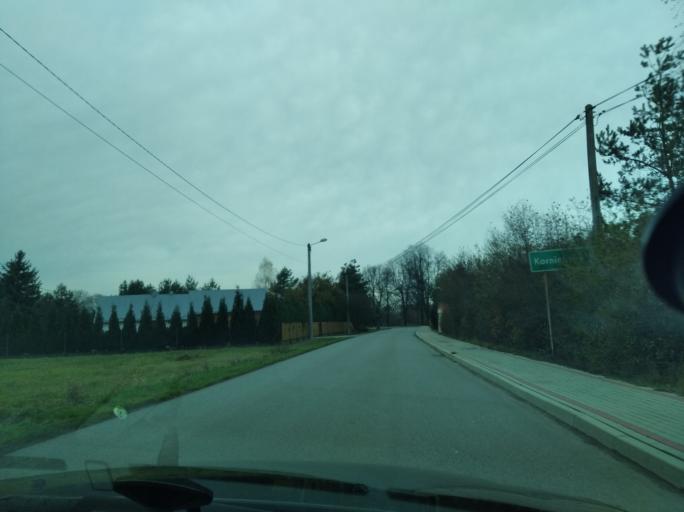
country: PL
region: Subcarpathian Voivodeship
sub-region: Powiat lancucki
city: Rogozno
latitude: 50.0994
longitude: 22.3790
